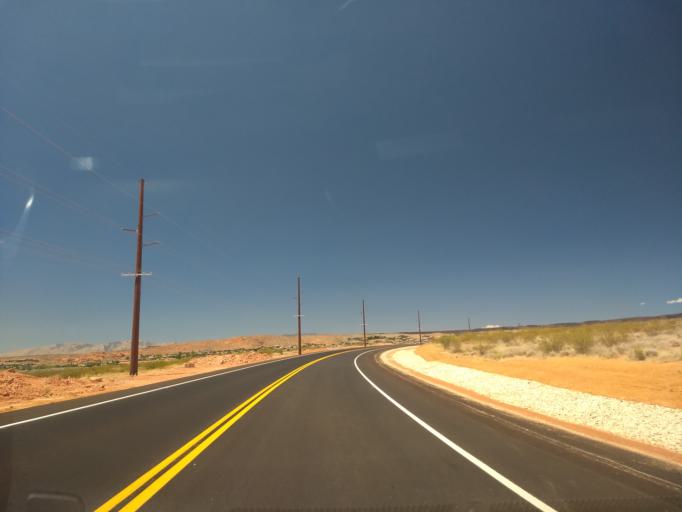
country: US
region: Utah
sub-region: Washington County
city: Washington
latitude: 37.1484
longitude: -113.5119
